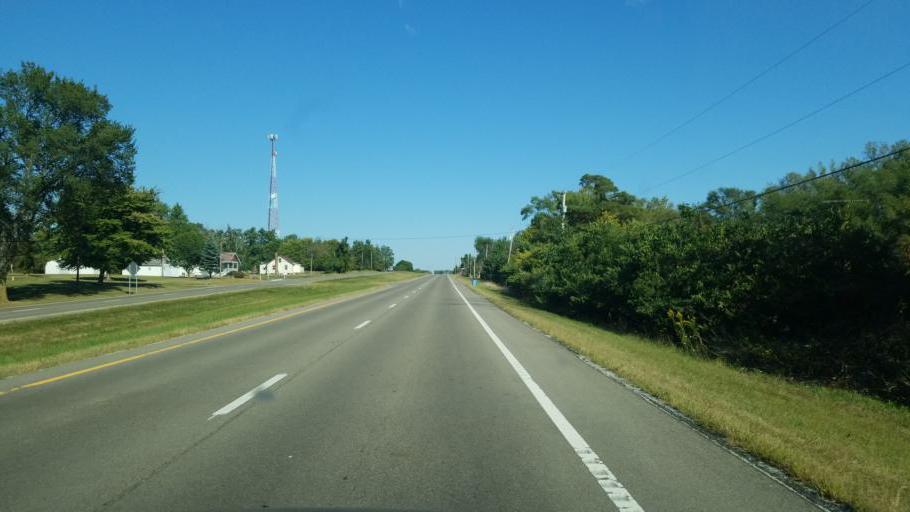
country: US
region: Ohio
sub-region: Clark County
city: Lisbon
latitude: 39.9262
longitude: -83.6430
